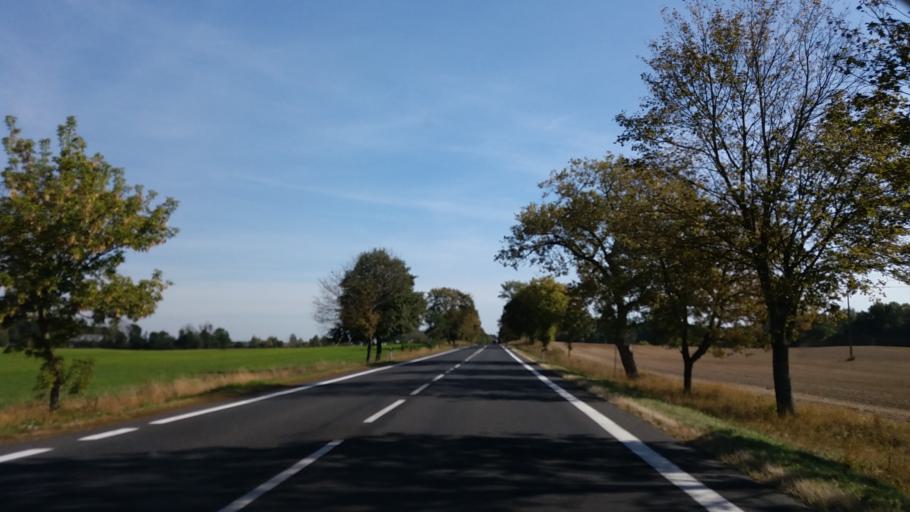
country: PL
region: Greater Poland Voivodeship
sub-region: Powiat miedzychodzki
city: Kwilcz
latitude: 52.5460
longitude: 16.1177
